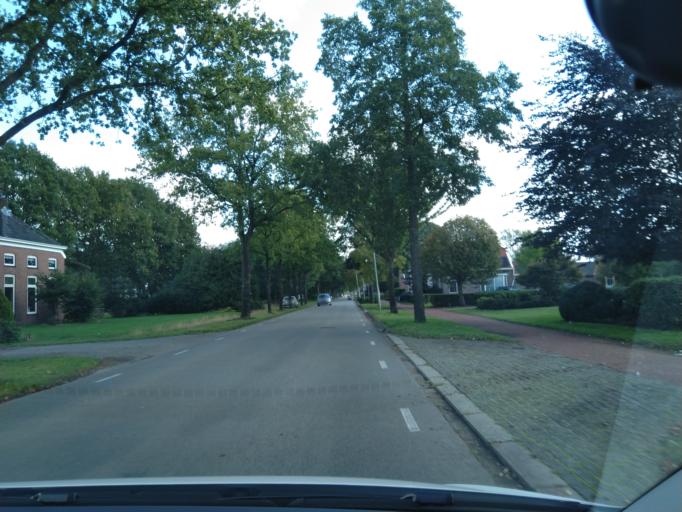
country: NL
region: Groningen
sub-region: Gemeente Veendam
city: Veendam
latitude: 53.0955
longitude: 6.9238
